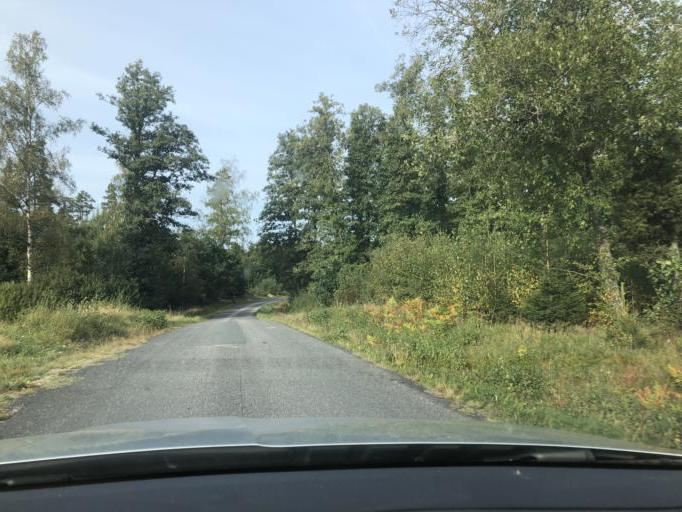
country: SE
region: Joenkoeping
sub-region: Vetlanda Kommun
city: Ekenassjon
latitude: 57.4909
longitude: 14.8935
